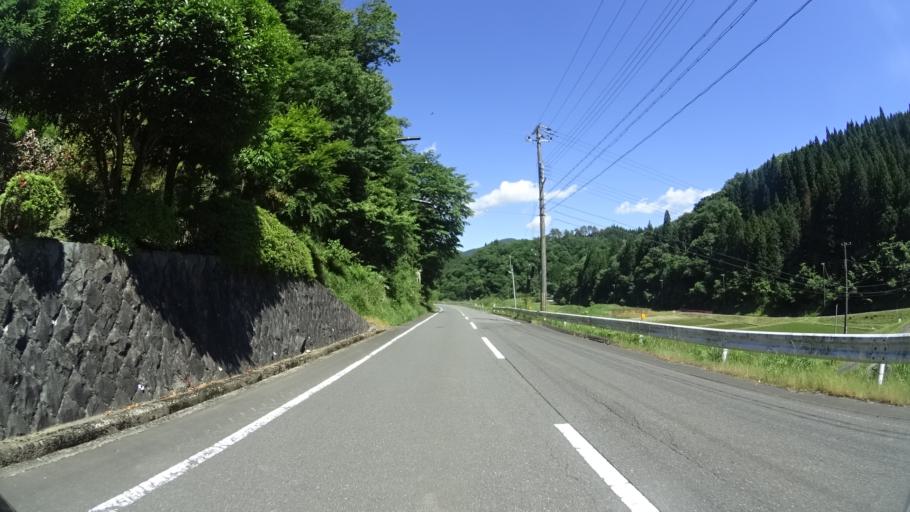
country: JP
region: Kyoto
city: Fukuchiyama
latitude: 35.4241
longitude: 135.0600
